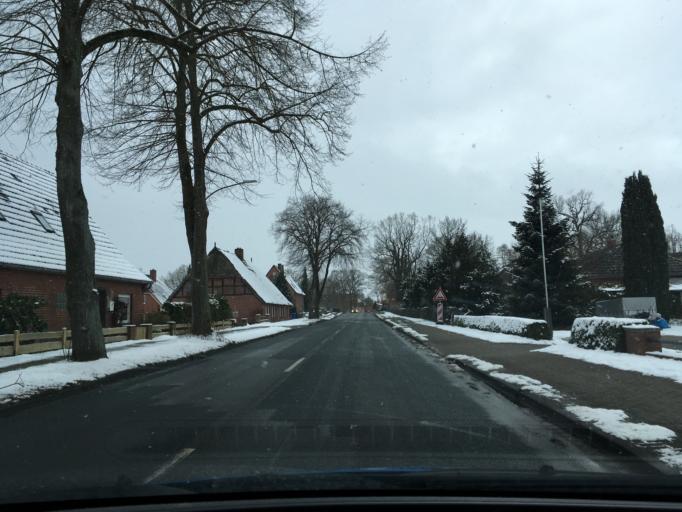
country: DE
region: Lower Saxony
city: Garstedt
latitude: 53.3043
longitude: 10.1811
